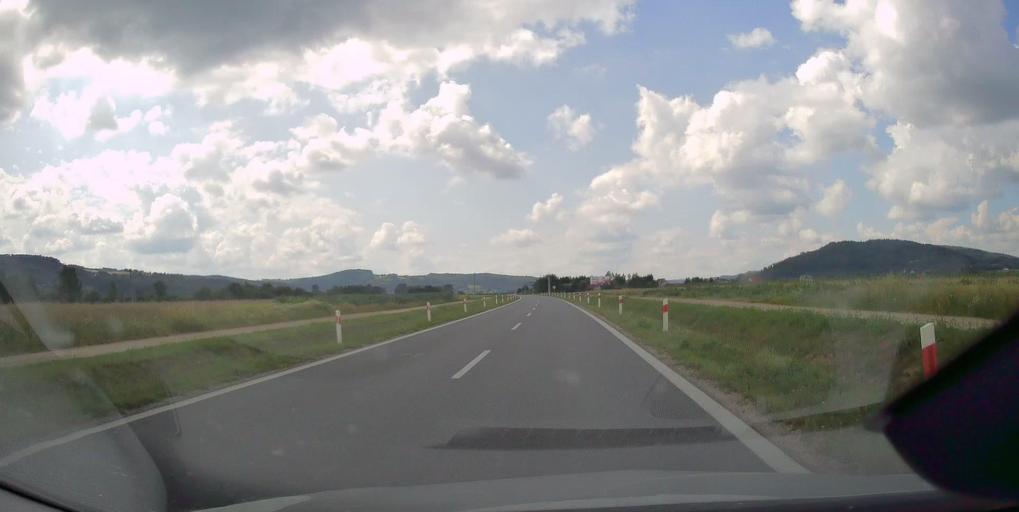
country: PL
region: Lesser Poland Voivodeship
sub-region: Powiat tarnowski
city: Wojnicz
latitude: 49.9412
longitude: 20.8451
